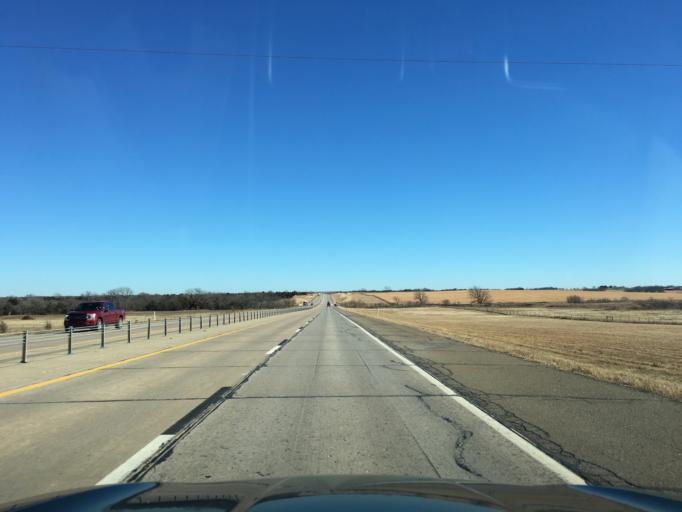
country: US
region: Oklahoma
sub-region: Pawnee County
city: Pawnee
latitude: 36.2251
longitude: -96.8546
